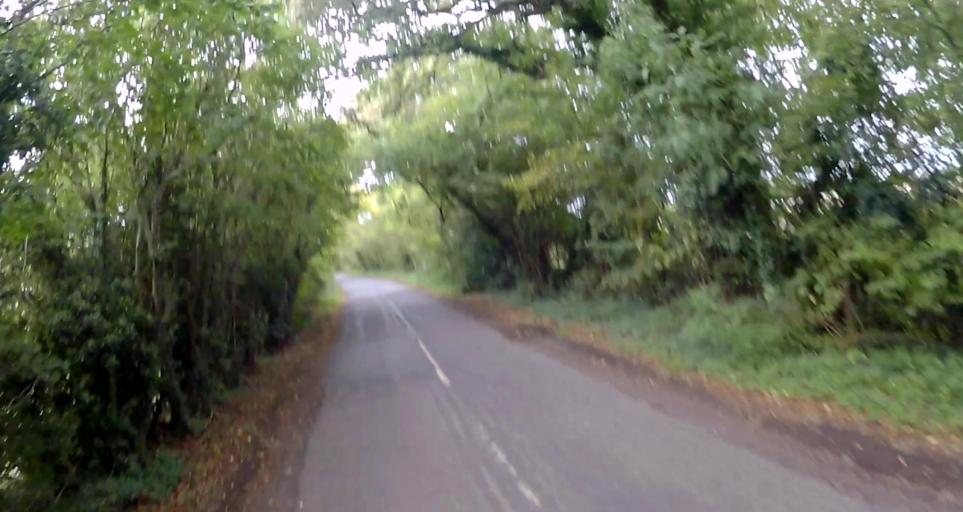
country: GB
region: England
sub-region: Hampshire
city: Four Marks
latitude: 51.1446
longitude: -1.0869
